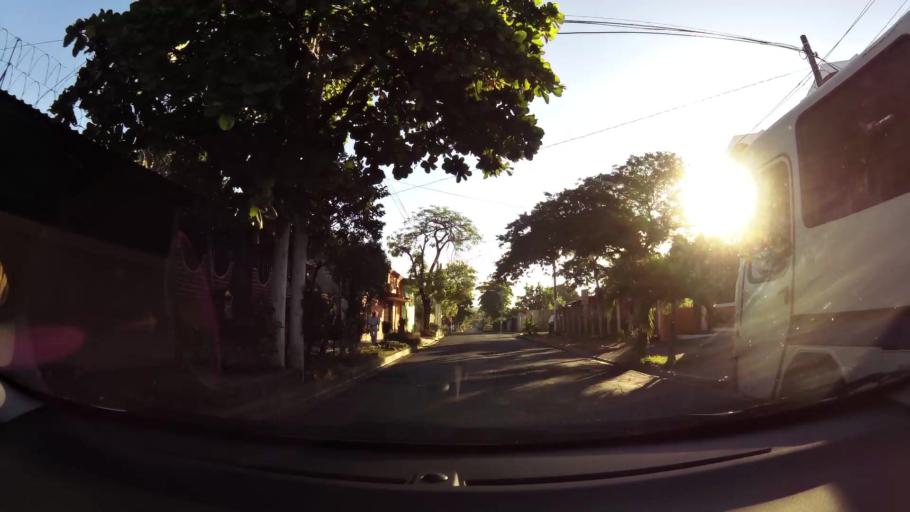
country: SV
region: San Miguel
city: San Miguel
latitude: 13.4873
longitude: -88.1717
